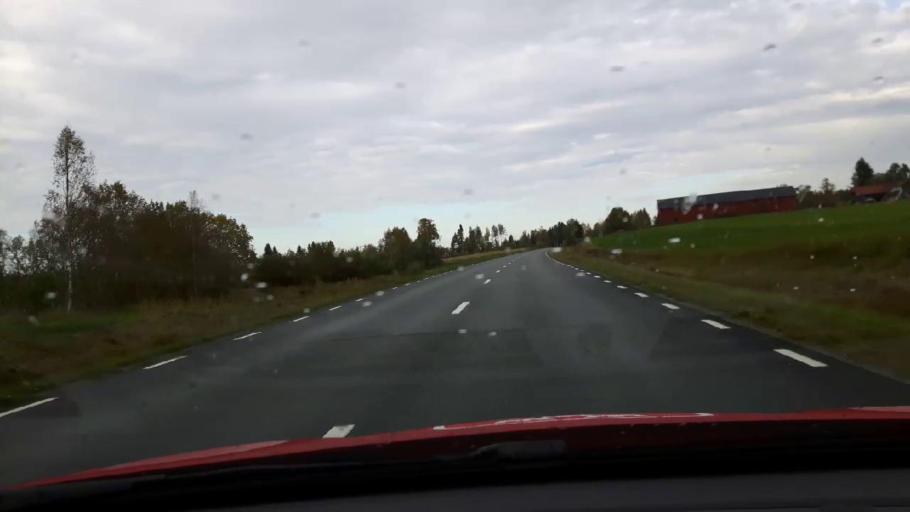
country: SE
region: Jaemtland
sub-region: Krokoms Kommun
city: Krokom
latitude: 63.1102
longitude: 14.2939
